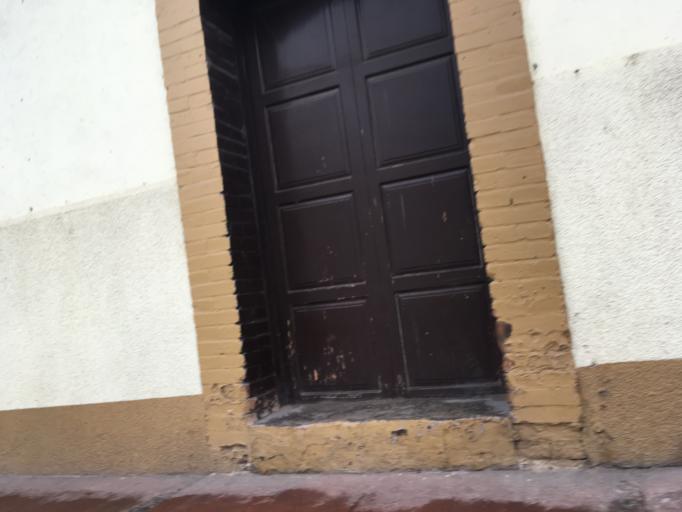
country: MX
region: Puebla
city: Chignahuapan
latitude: 19.8396
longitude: -98.0329
